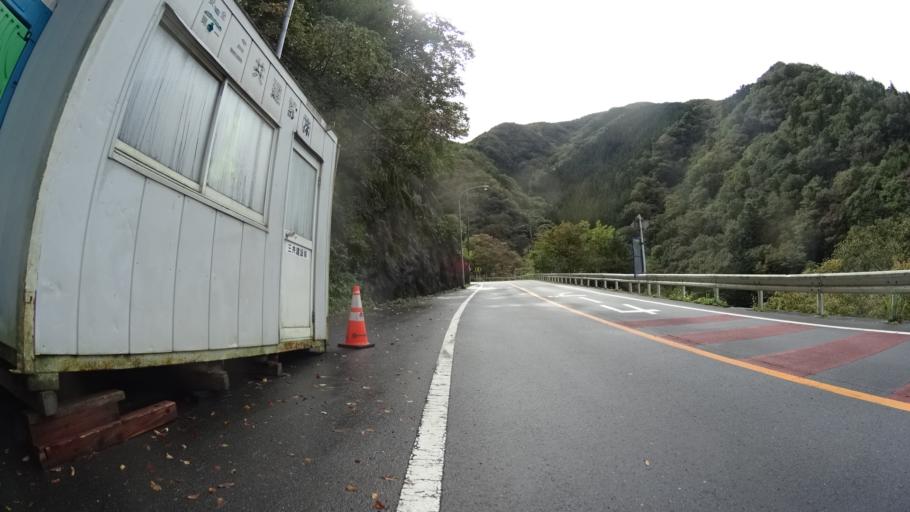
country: JP
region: Yamanashi
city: Otsuki
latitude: 35.7870
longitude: 138.9656
